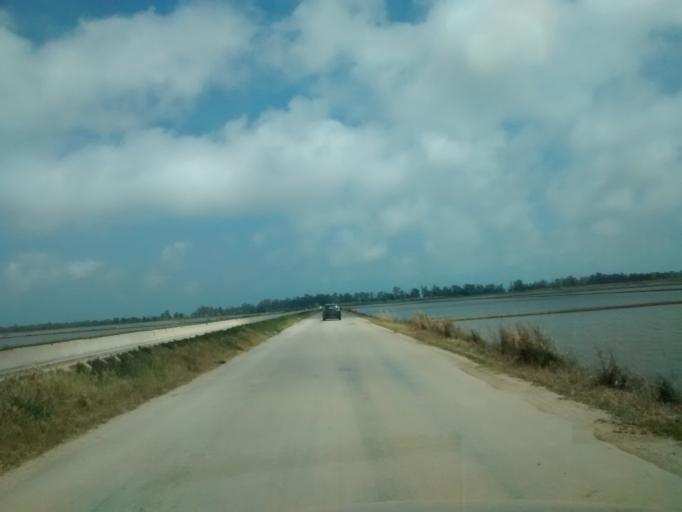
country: ES
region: Catalonia
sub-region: Provincia de Tarragona
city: Deltebre
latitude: 40.7000
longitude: 0.8135
